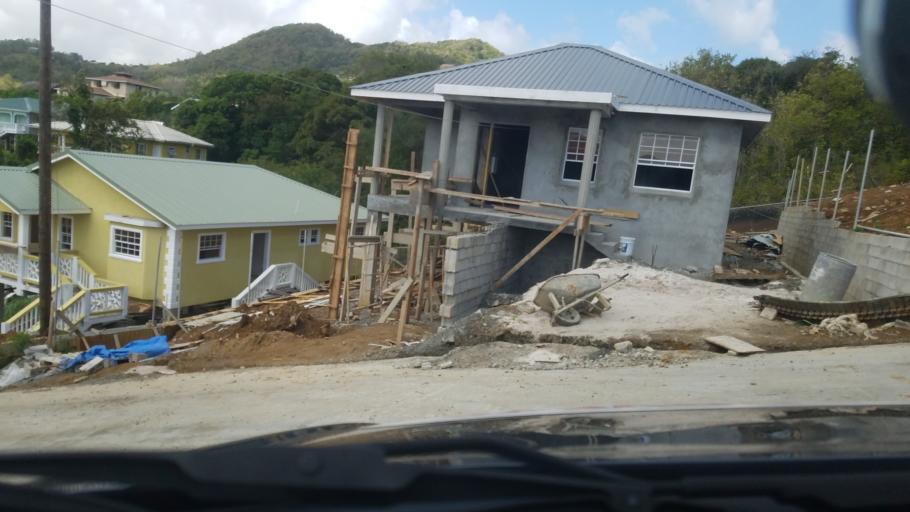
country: LC
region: Gros-Islet
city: Gros Islet
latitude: 14.0619
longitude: -60.9468
